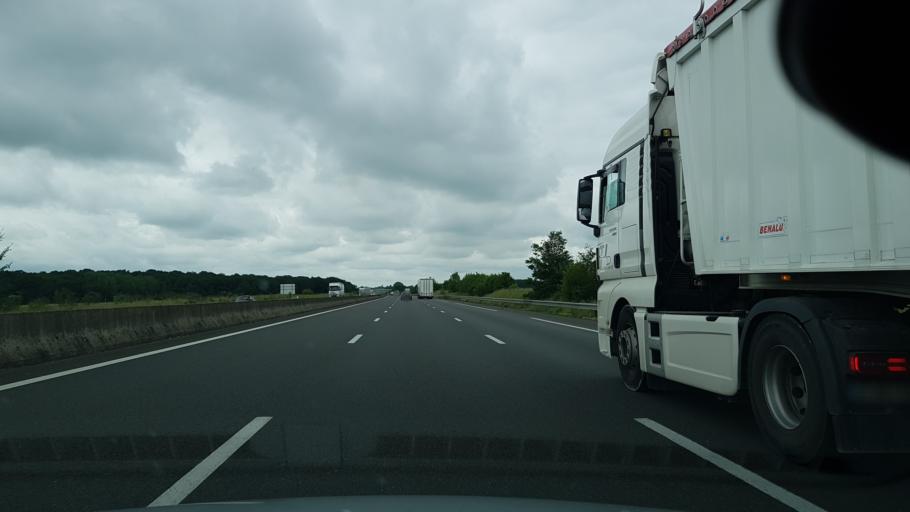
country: FR
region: Centre
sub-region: Departement du Loir-et-Cher
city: Herbault
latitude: 47.6011
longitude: 1.1085
